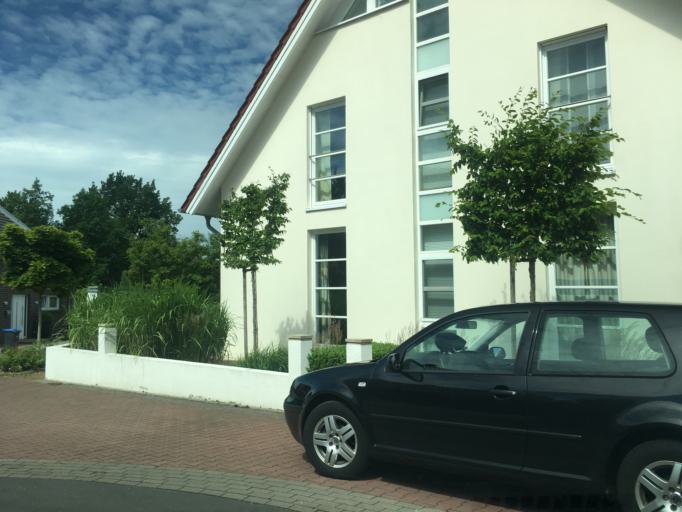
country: DE
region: North Rhine-Westphalia
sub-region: Regierungsbezirk Munster
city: Altenberge
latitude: 52.0558
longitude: 7.4762
